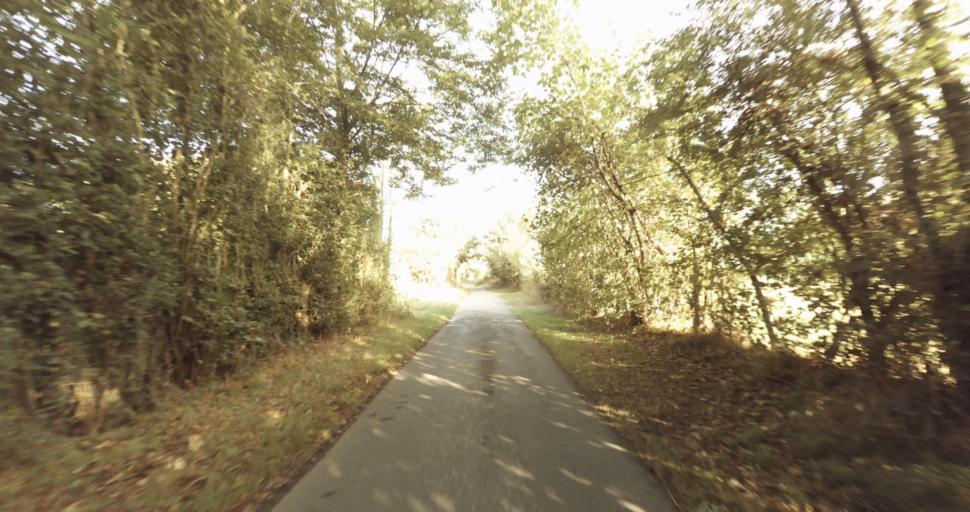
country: FR
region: Lower Normandy
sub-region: Departement de l'Orne
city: Vimoutiers
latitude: 48.8799
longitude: 0.2483
